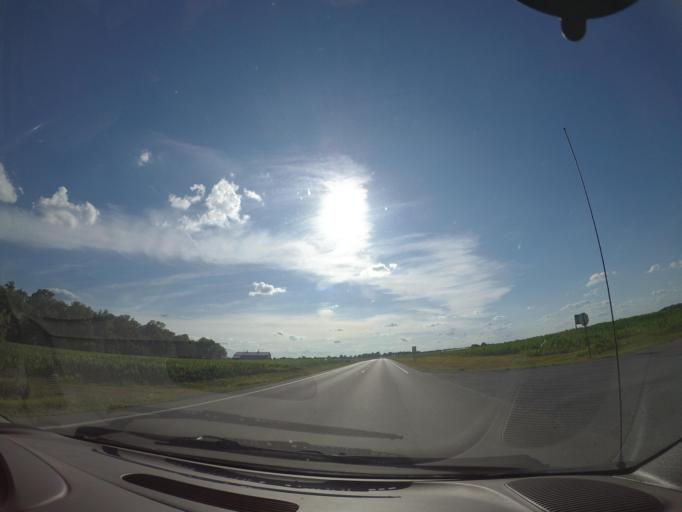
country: US
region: Ohio
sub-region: Henry County
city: Napoleon
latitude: 41.4321
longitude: -84.2211
